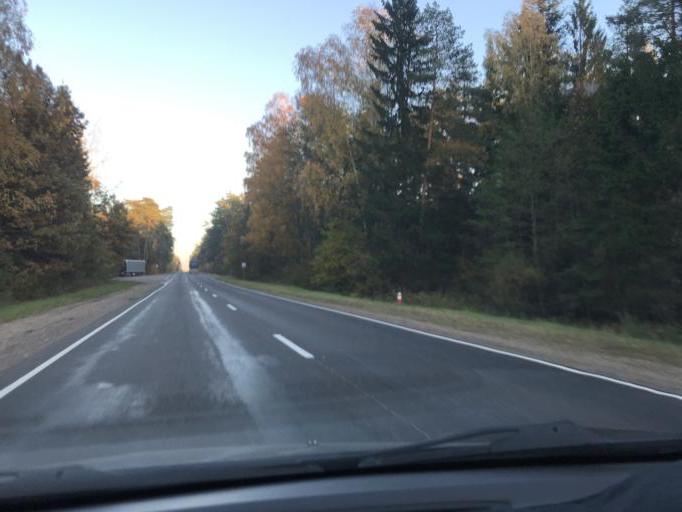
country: BY
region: Minsk
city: Staryya Darohi
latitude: 53.0411
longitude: 28.1653
